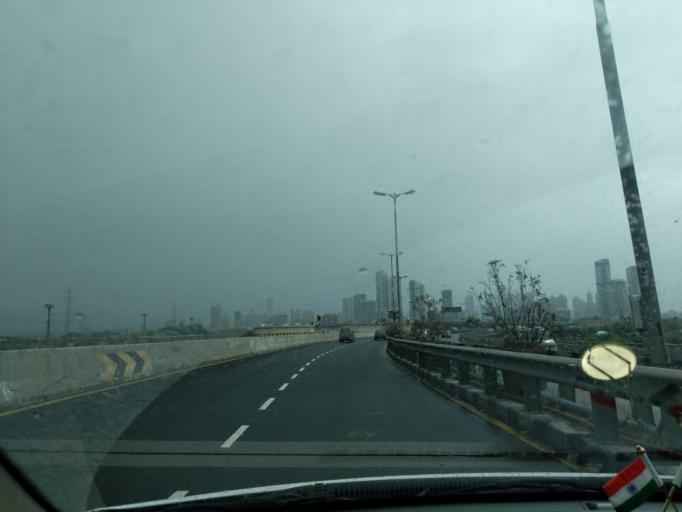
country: IN
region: Maharashtra
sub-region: Mumbai Suburban
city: Mumbai
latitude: 19.0113
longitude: 72.8697
